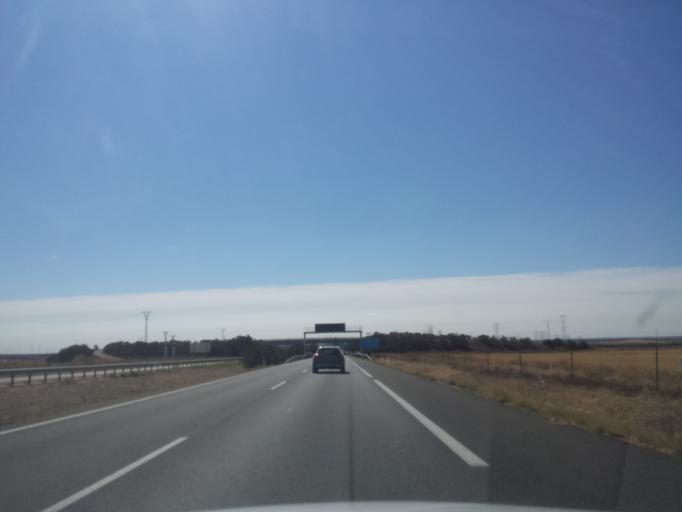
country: ES
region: Castille and Leon
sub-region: Provincia de Valladolid
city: Tordesillas
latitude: 41.5185
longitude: -5.0319
